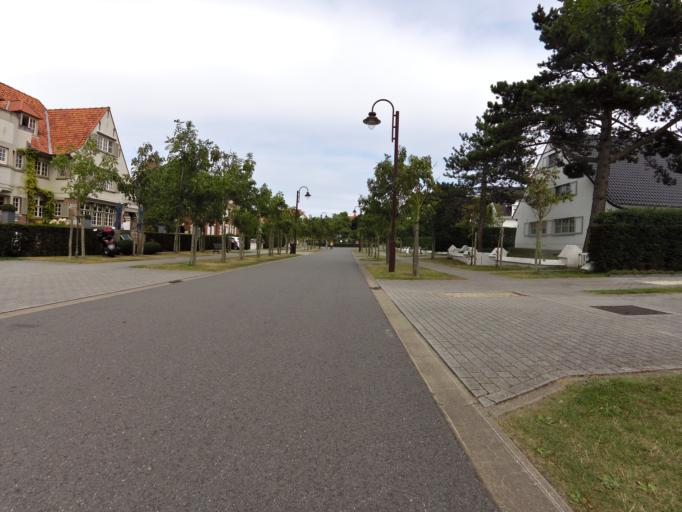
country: BE
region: Flanders
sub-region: Provincie West-Vlaanderen
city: De Haan
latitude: 51.2767
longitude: 3.0355
